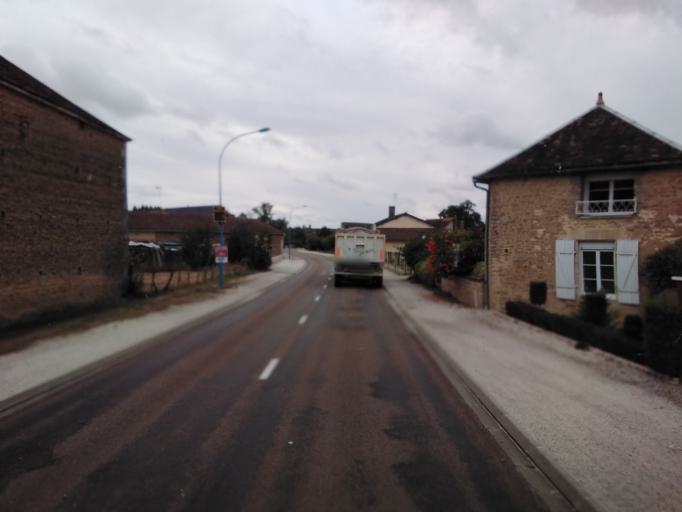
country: FR
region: Champagne-Ardenne
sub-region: Departement de l'Aube
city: Vendeuvre-sur-Barse
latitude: 48.2992
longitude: 4.5176
